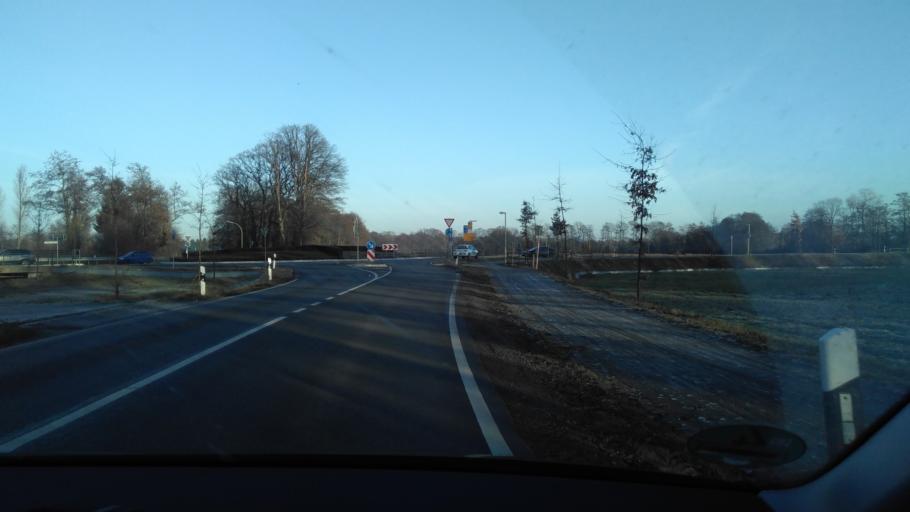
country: DE
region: North Rhine-Westphalia
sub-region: Regierungsbezirk Detmold
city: Verl
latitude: 51.8852
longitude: 8.5134
